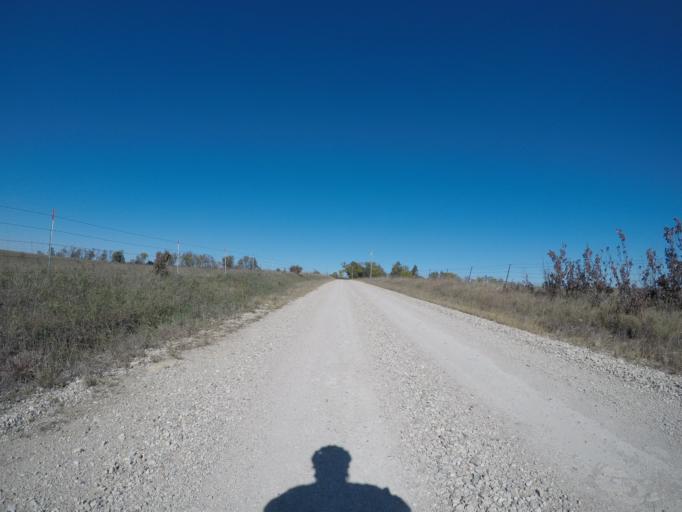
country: US
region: Kansas
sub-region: Wabaunsee County
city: Alma
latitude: 39.0563
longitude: -96.3582
